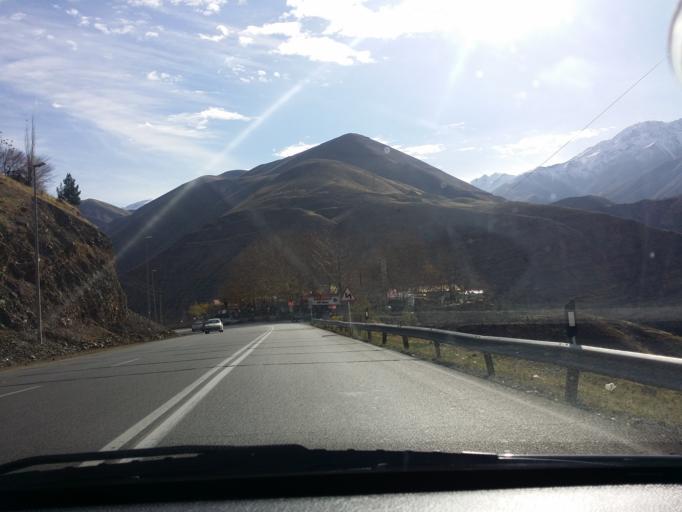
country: IR
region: Alborz
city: Karaj
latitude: 35.9452
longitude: 51.0735
